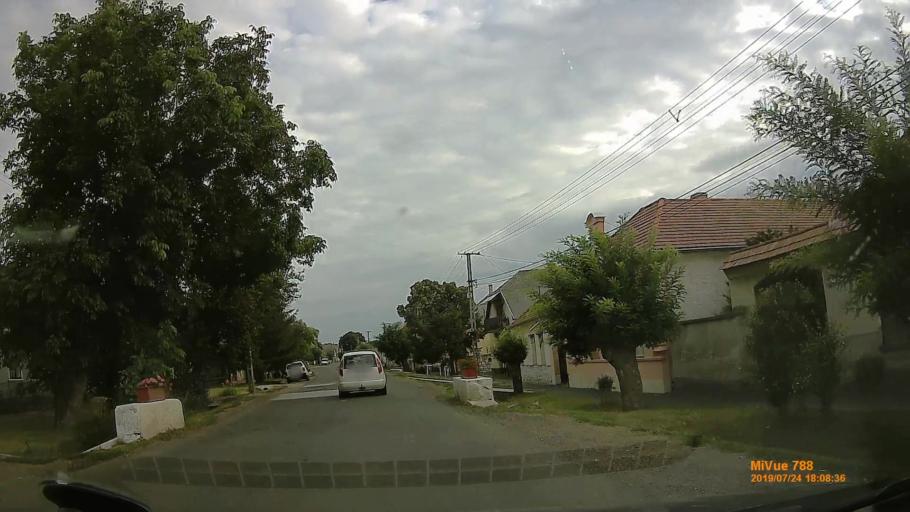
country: HU
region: Borsod-Abauj-Zemplen
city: Abaujszanto
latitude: 48.2740
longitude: 21.1852
